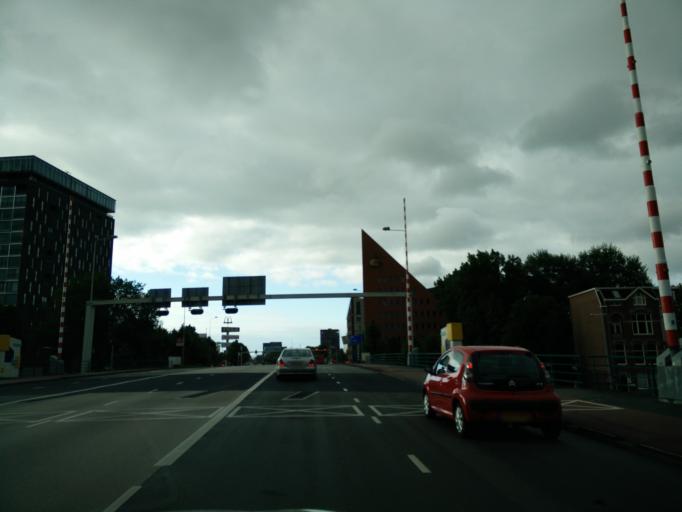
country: NL
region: Groningen
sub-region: Gemeente Groningen
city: Oosterpark
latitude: 53.2173
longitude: 6.5797
